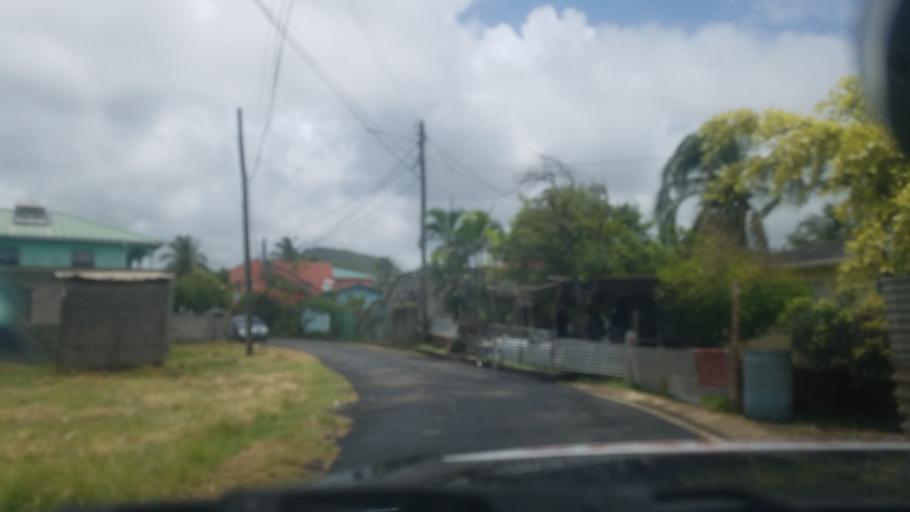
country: LC
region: Vieux-Fort
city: Vieux Fort
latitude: 13.7421
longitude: -60.9555
